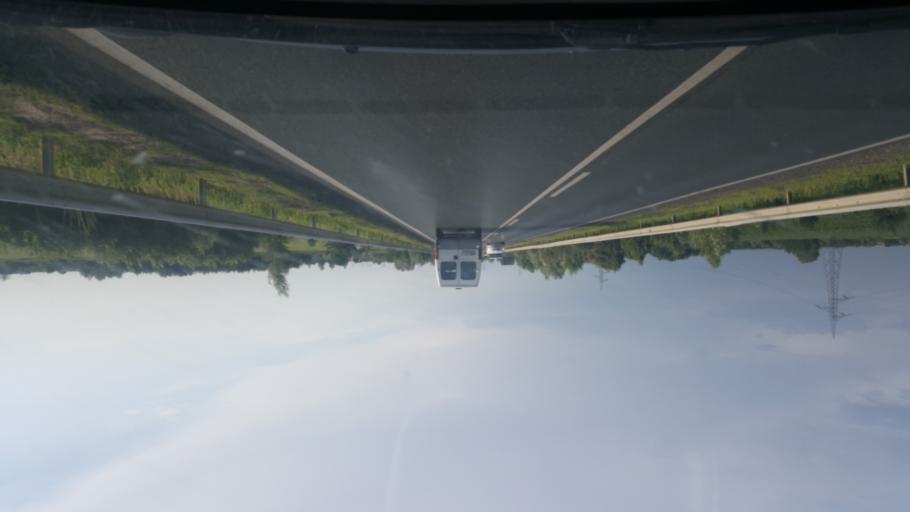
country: HU
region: Pest
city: Ullo
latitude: 47.3897
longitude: 19.3677
